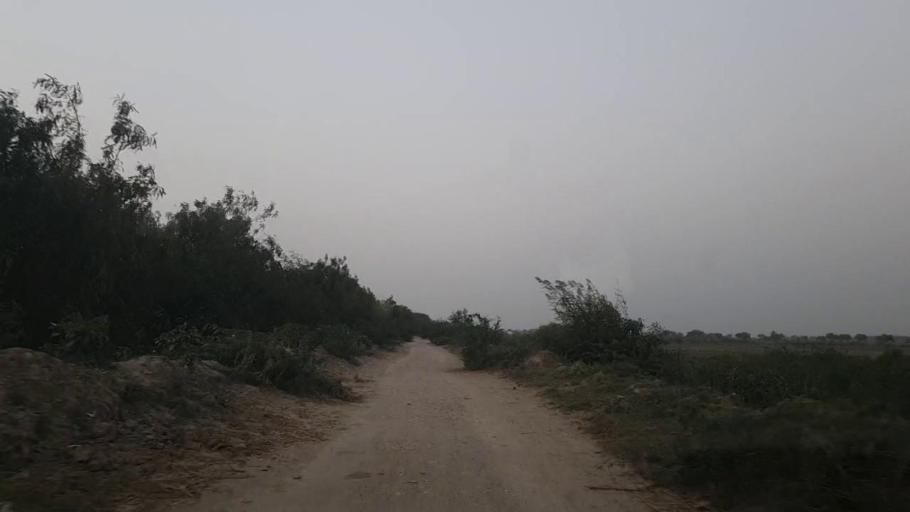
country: PK
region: Sindh
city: Mirpur Sakro
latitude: 24.5812
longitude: 67.7852
